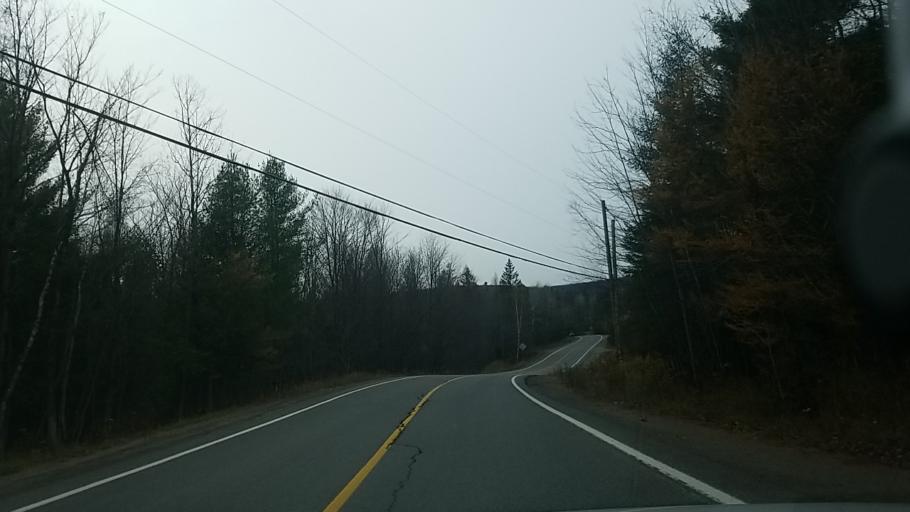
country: CA
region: Quebec
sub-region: Laurentides
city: Saint-Colomban
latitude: 45.7898
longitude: -74.1280
